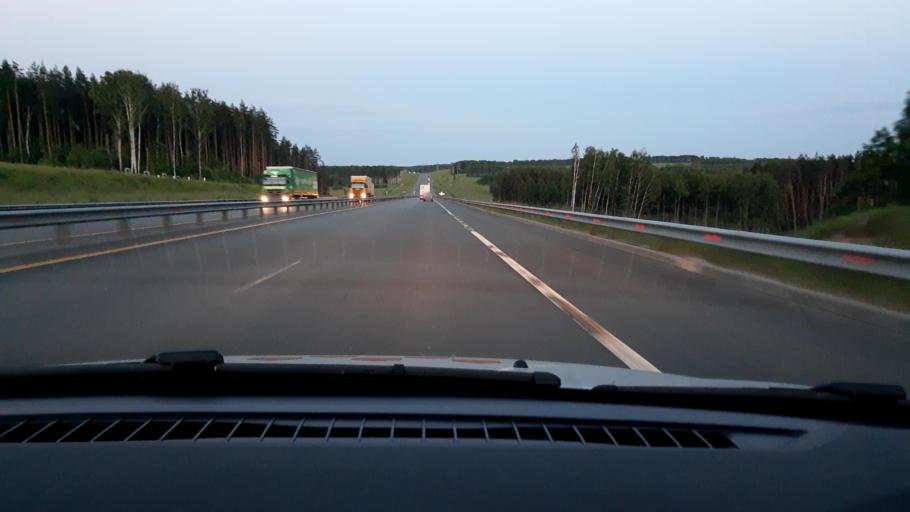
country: RU
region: Nizjnij Novgorod
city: Kstovo
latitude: 56.0826
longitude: 44.0940
